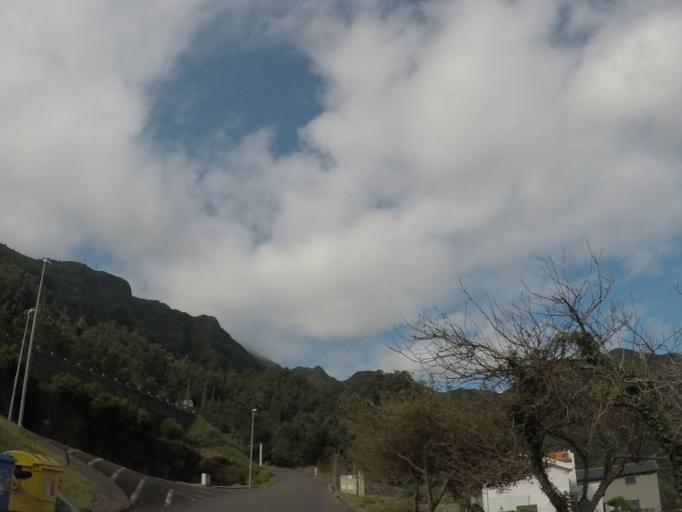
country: PT
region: Madeira
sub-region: Sao Vicente
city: Sao Vicente
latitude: 32.7800
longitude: -17.0449
